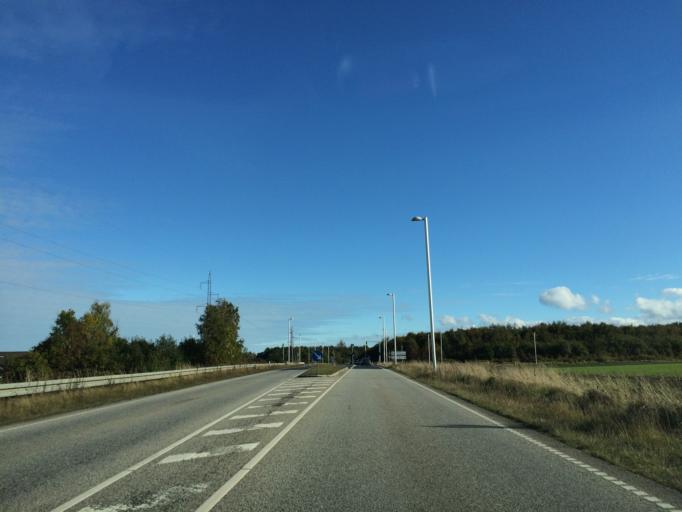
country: DK
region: Central Jutland
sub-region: Randers Kommune
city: Randers
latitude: 56.4384
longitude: 10.0703
